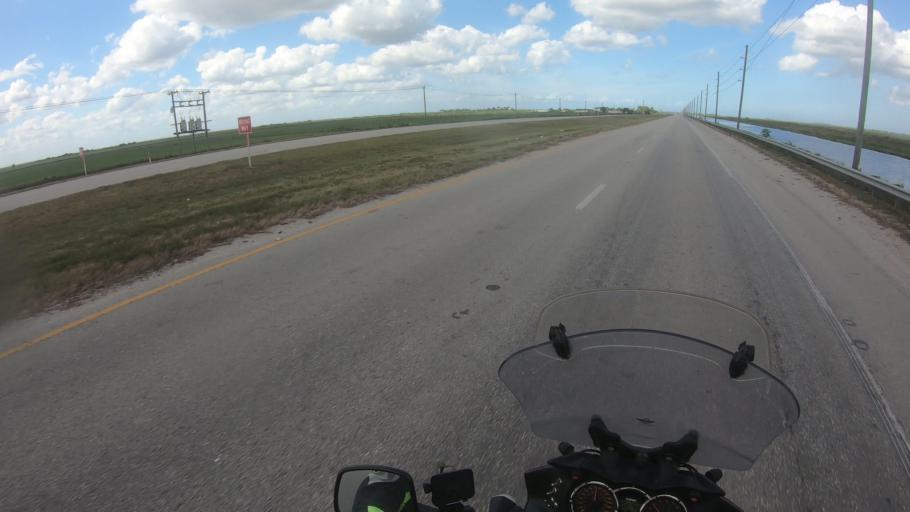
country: US
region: Florida
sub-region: Palm Beach County
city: South Bay
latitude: 26.6115
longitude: -80.7110
